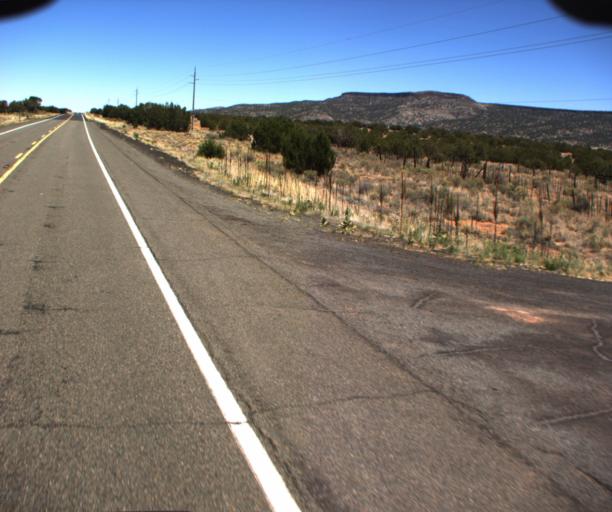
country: US
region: Arizona
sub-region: Coconino County
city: LeChee
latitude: 34.8301
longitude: -110.9521
